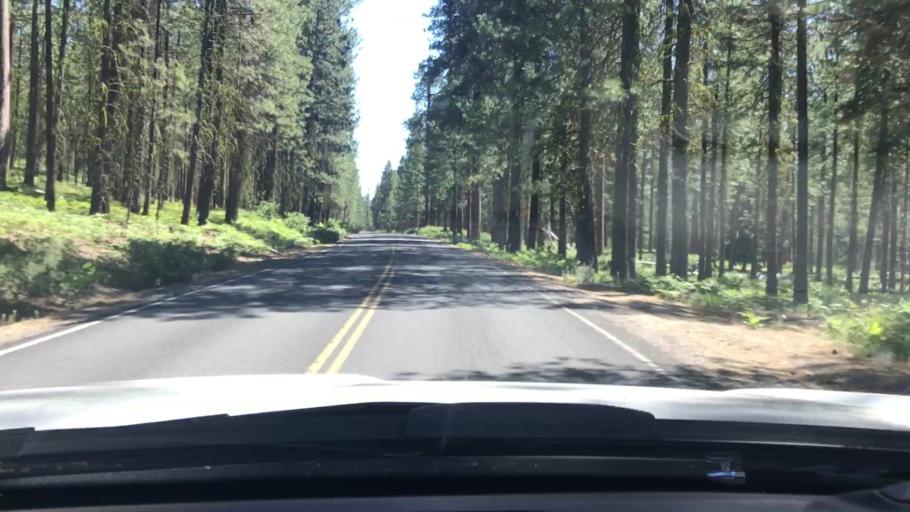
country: US
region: Oregon
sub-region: Deschutes County
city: Sisters
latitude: 44.4096
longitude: -121.6736
